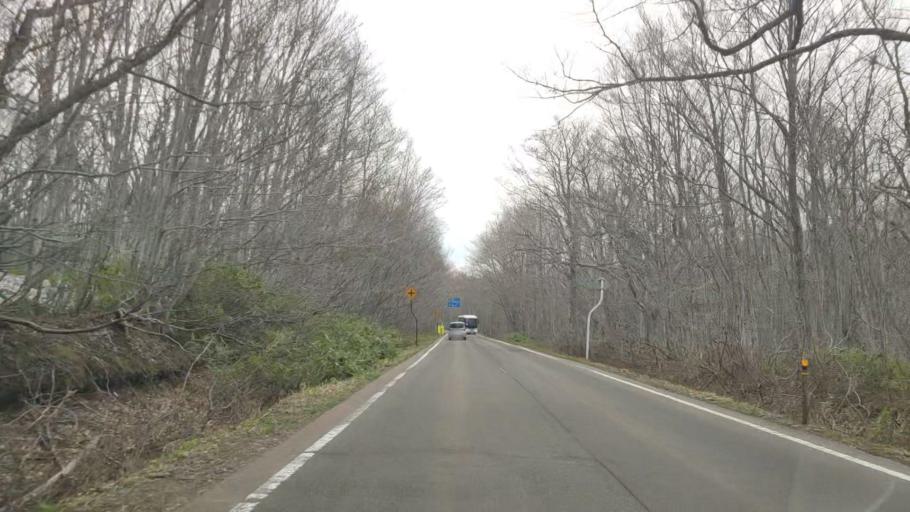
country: JP
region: Aomori
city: Aomori Shi
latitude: 40.6653
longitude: 140.9567
